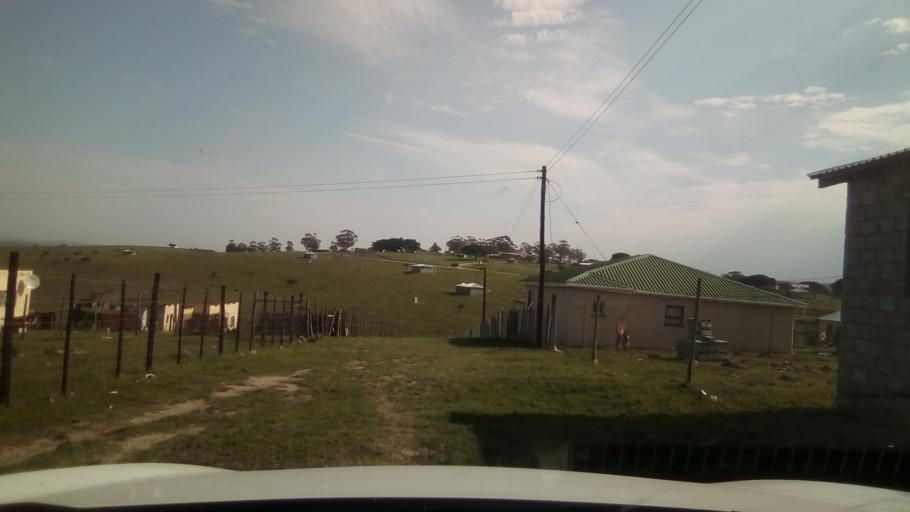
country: ZA
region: Eastern Cape
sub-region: Buffalo City Metropolitan Municipality
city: Bhisho
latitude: -32.9873
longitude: 27.2655
